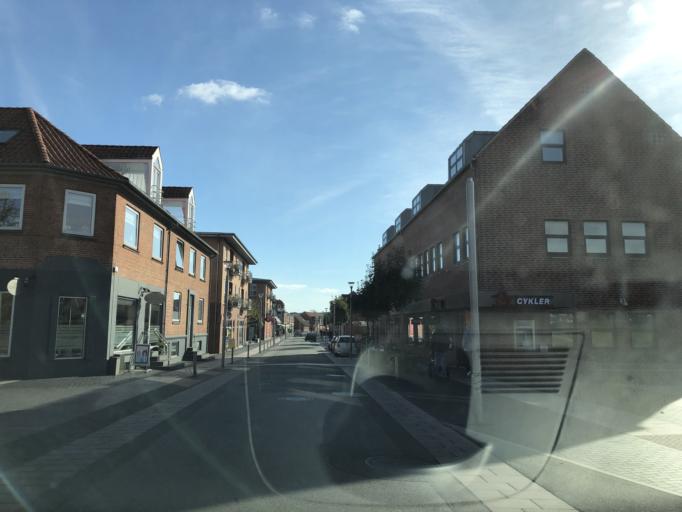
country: DK
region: Central Jutland
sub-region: Syddjurs Kommune
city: Hornslet
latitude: 56.3174
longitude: 10.3168
